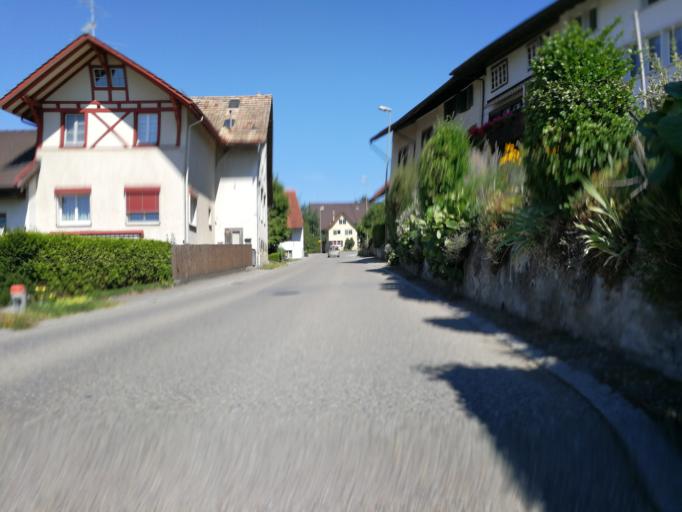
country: CH
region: Zurich
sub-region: Bezirk Hinwil
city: Gossau
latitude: 47.3265
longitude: 8.7469
